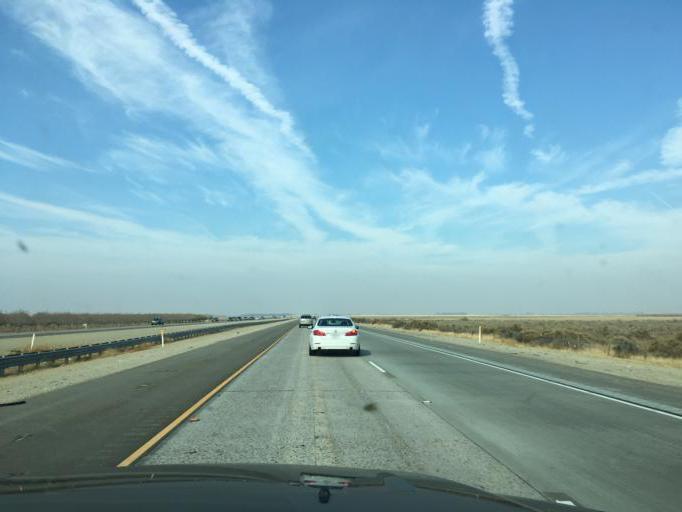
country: US
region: California
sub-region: Kern County
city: Lost Hills
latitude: 35.5404
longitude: -119.5786
